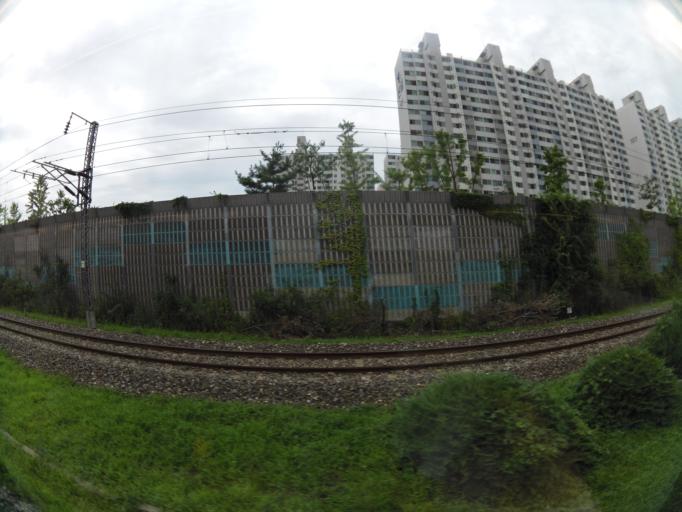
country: KR
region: Gyeonggi-do
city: Suwon-si
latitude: 37.3006
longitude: 126.9678
